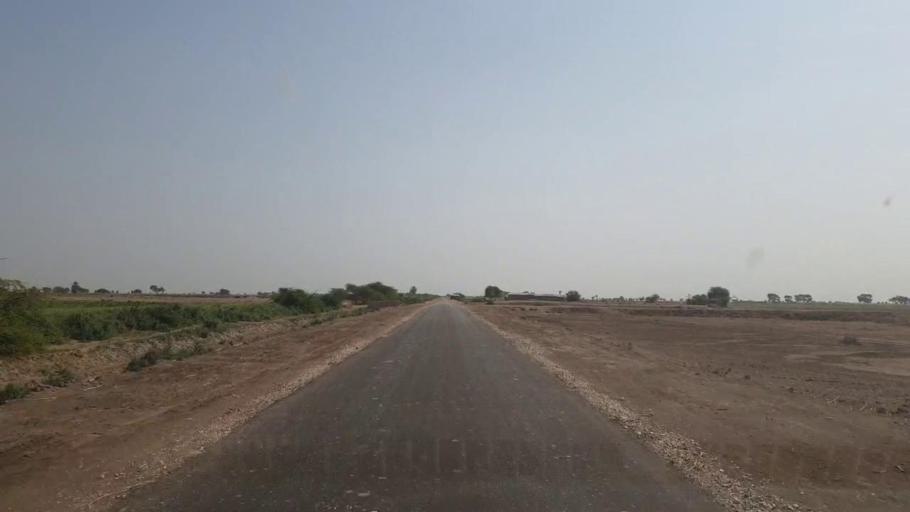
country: PK
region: Sindh
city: Jati
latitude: 24.4615
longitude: 68.5116
